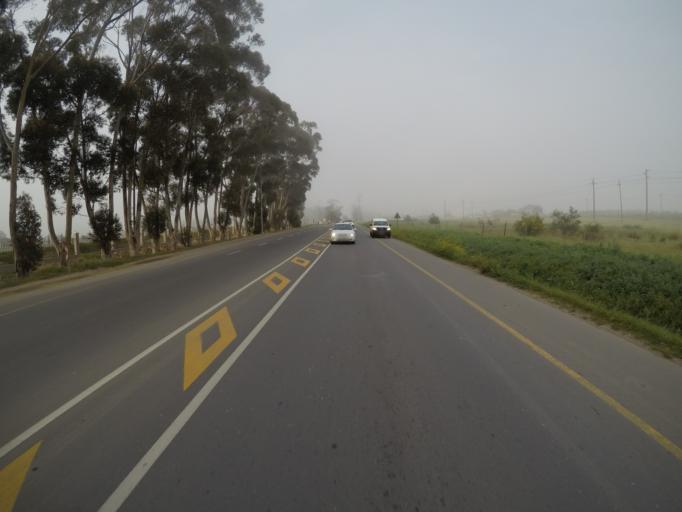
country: ZA
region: Western Cape
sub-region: City of Cape Town
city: Kraaifontein
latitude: -33.7908
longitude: 18.6976
